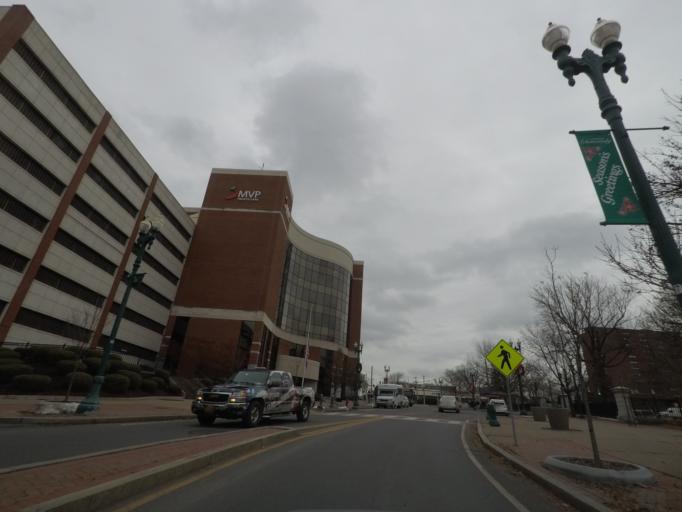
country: US
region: New York
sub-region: Schenectady County
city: Schenectady
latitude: 42.8112
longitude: -73.9389
